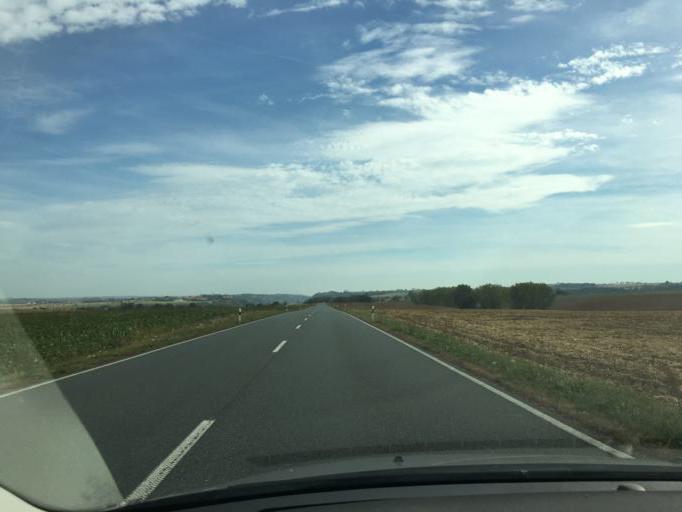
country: DE
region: Saxony
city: Lommatzsch
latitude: 51.2091
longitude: 13.3817
